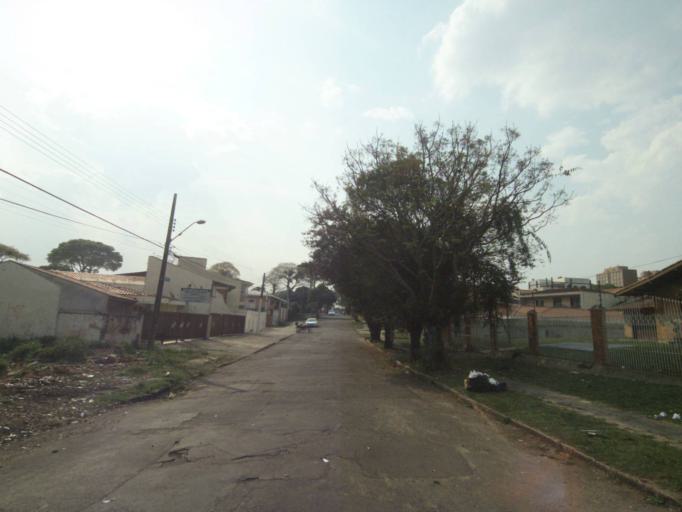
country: BR
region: Parana
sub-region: Curitiba
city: Curitiba
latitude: -25.4594
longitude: -49.2688
